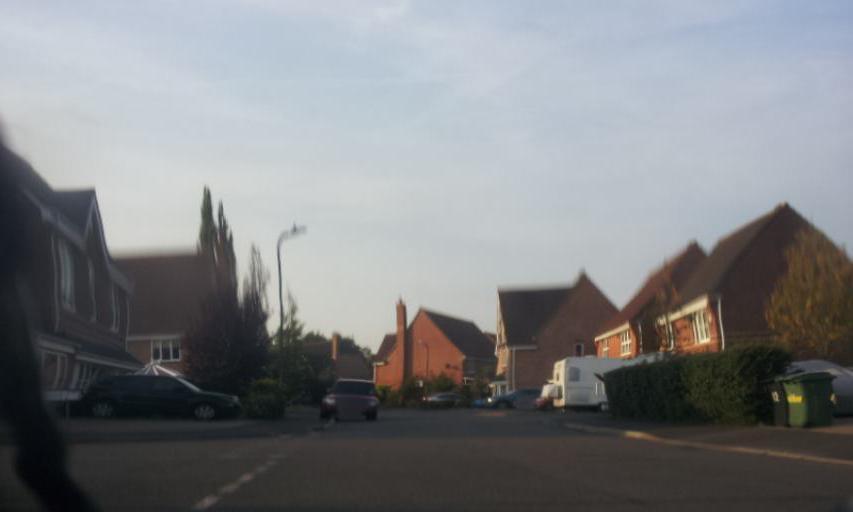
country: GB
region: England
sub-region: Kent
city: Maidstone
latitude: 51.2897
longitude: 0.5042
